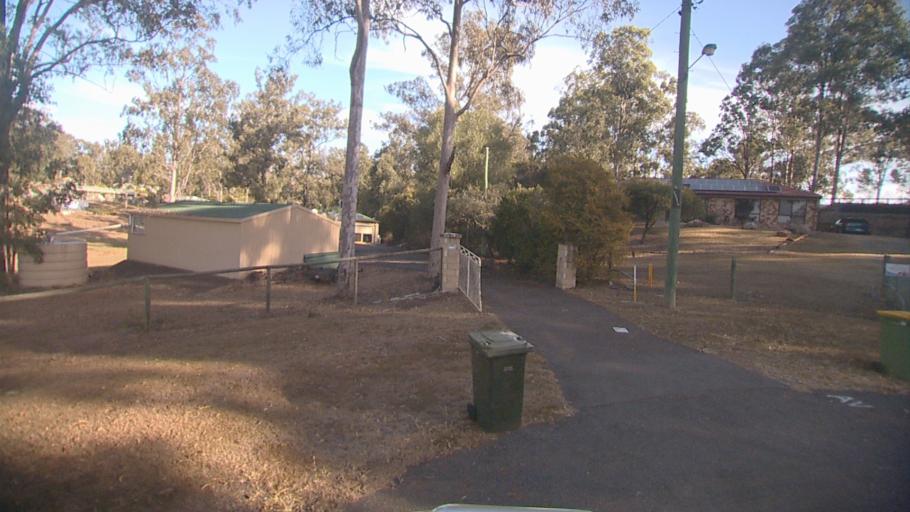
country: AU
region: Queensland
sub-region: Logan
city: Cedar Vale
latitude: -27.8759
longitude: 153.0065
